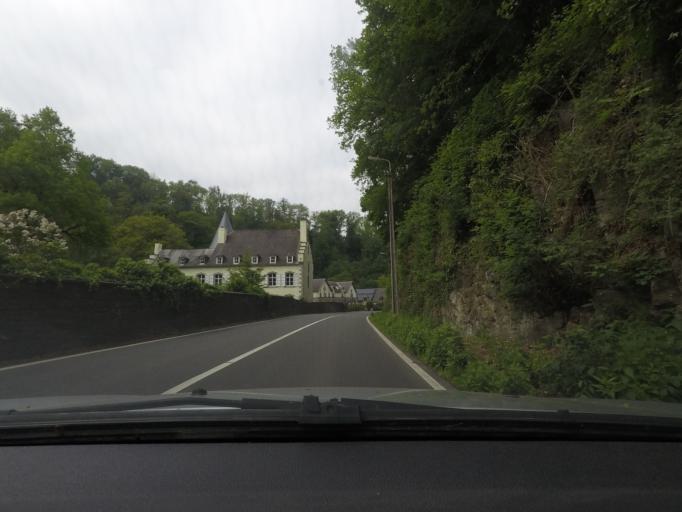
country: BE
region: Wallonia
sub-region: Province de Namur
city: Assesse
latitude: 50.4547
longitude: 5.0016
